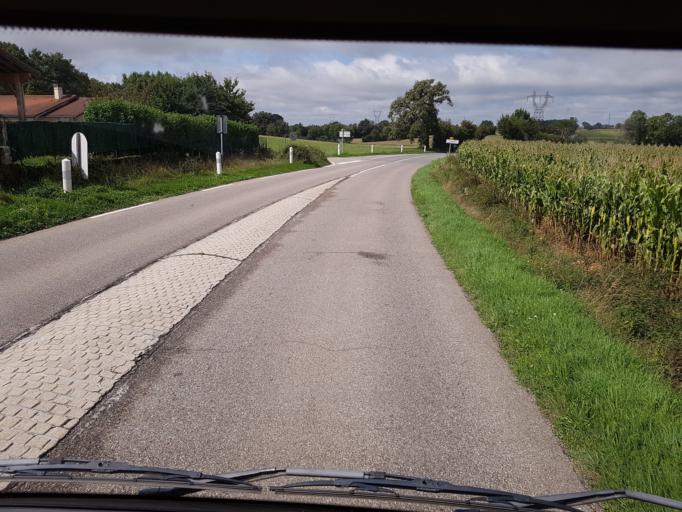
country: FR
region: Rhone-Alpes
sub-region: Departement de l'Ain
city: Perouges
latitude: 45.9076
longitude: 5.1656
